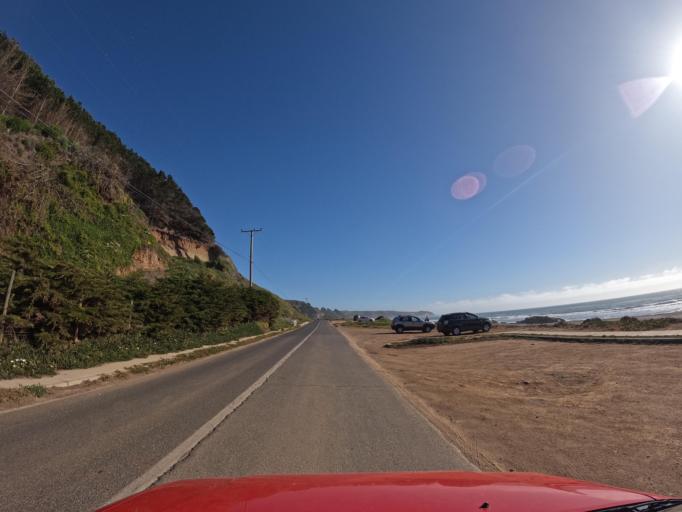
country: CL
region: Maule
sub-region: Provincia de Talca
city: Constitucion
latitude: -34.8611
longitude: -72.1470
